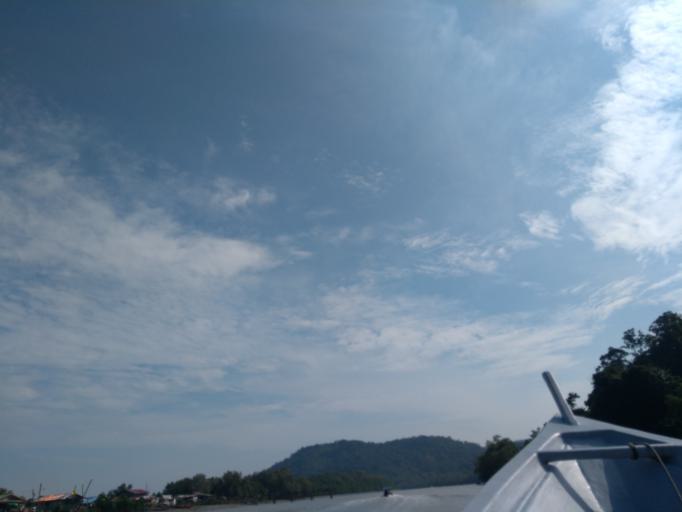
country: MY
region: Sarawak
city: Kuching
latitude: 1.6668
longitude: 110.4321
